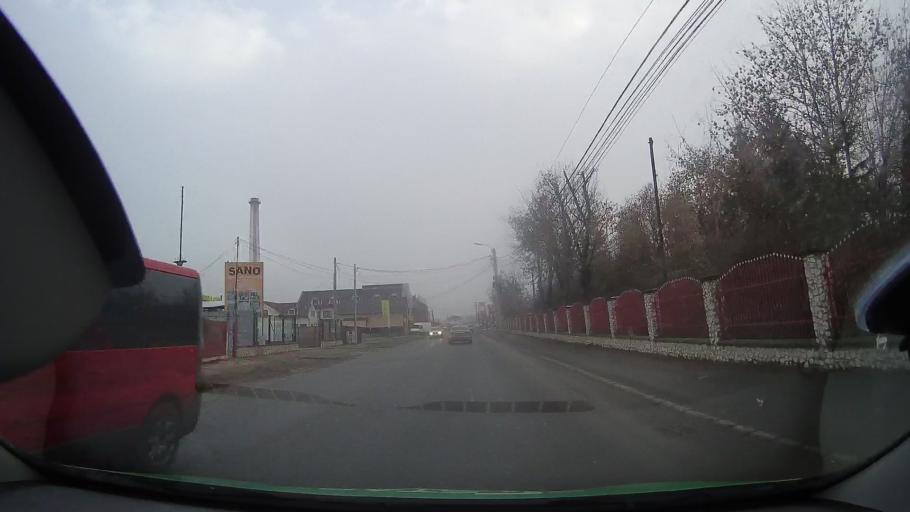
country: RO
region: Mures
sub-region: Municipiul Tarnaveni
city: Tarnaveni
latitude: 46.3171
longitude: 24.2969
